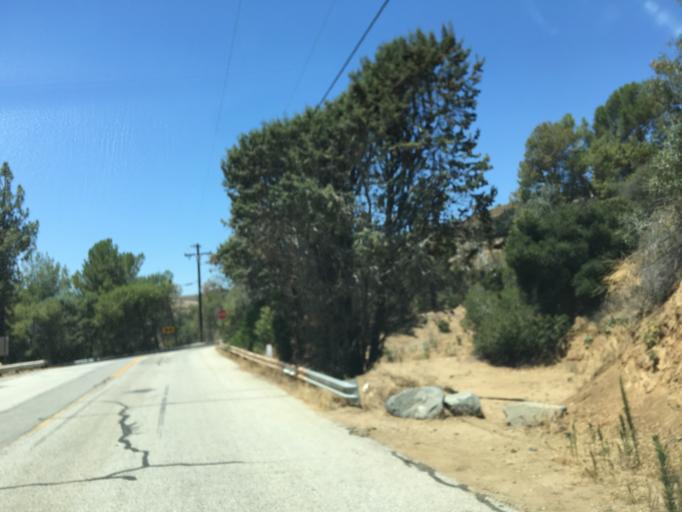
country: US
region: California
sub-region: Los Angeles County
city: Glendora
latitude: 34.1561
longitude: -117.8360
